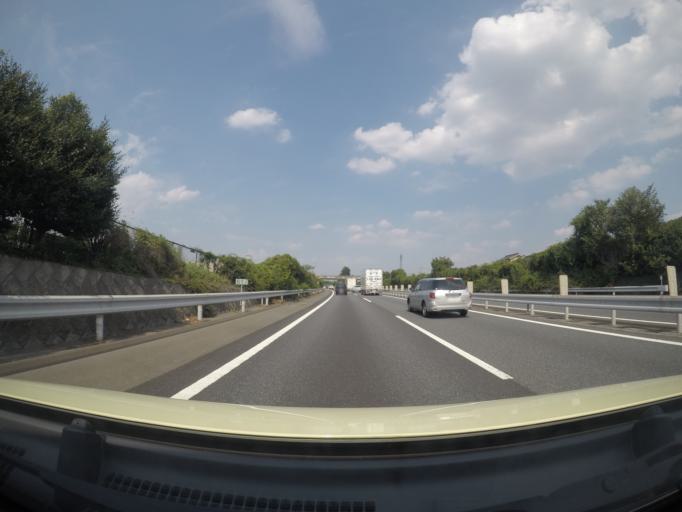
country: JP
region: Saitama
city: Hanno
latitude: 35.8077
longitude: 139.3521
